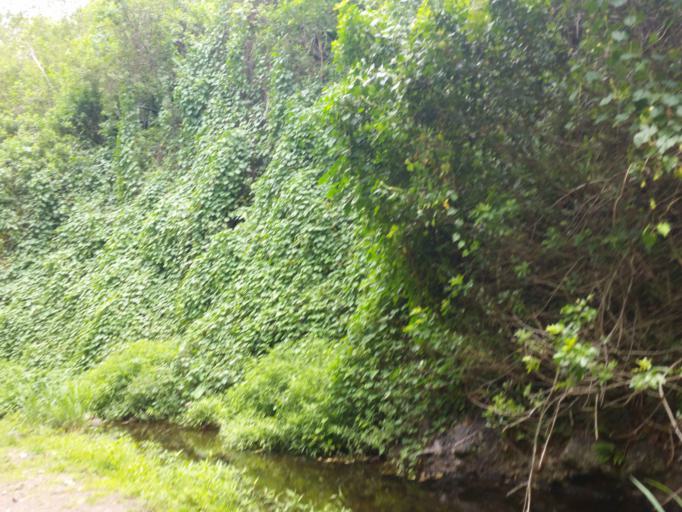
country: RE
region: Reunion
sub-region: Reunion
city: L'Entre-Deux
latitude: -21.2523
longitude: 55.4687
